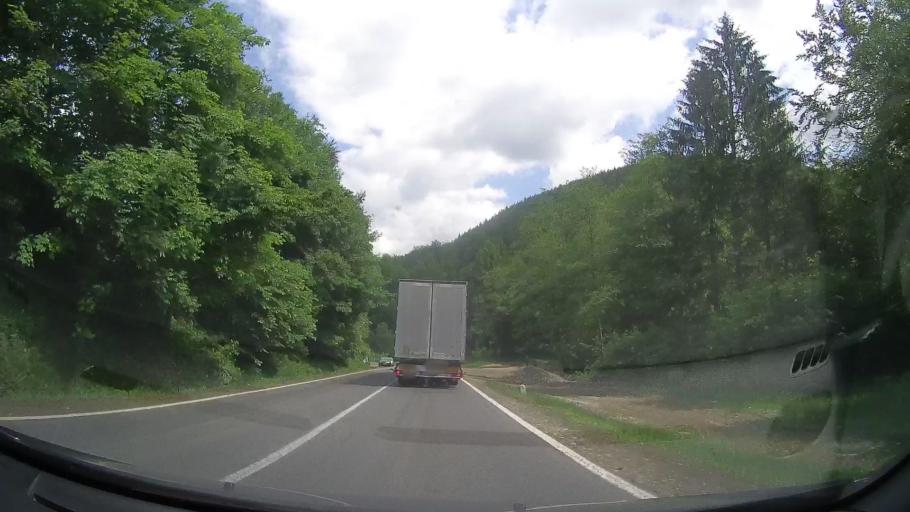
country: RO
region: Prahova
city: Maneciu
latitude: 45.3767
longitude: 25.9293
